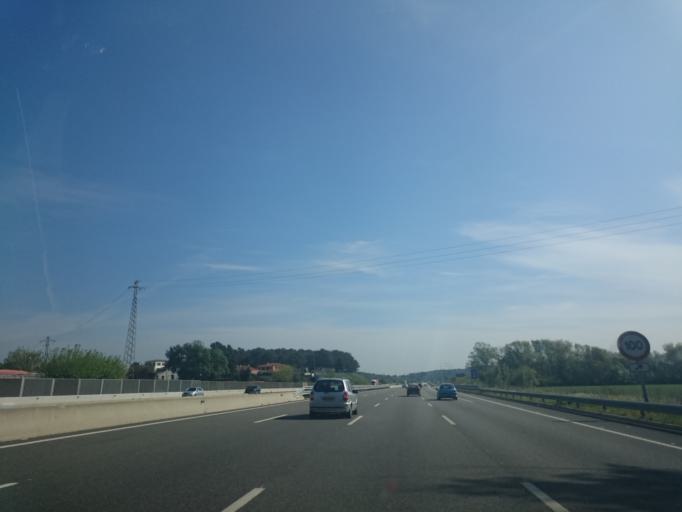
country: ES
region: Catalonia
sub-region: Provincia de Girona
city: Salt
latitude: 41.9904
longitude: 2.7890
